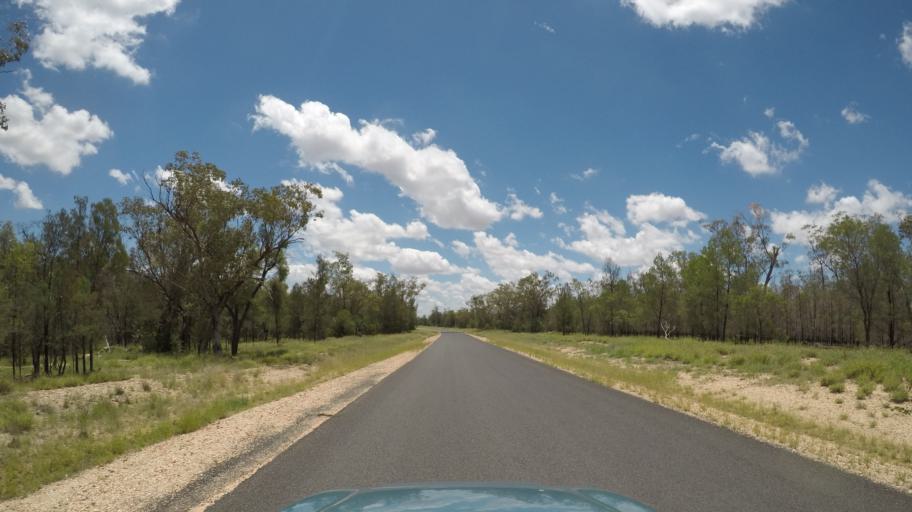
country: AU
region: Queensland
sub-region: Goondiwindi
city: Goondiwindi
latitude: -28.1558
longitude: 150.1215
